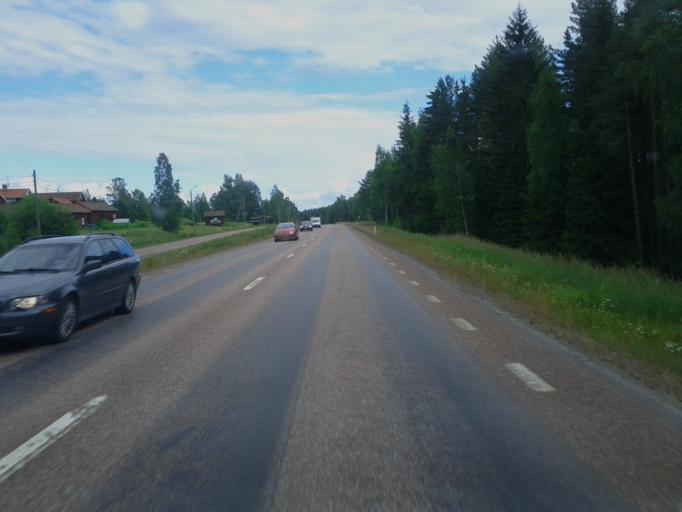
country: SE
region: Dalarna
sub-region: Faluns Kommun
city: Bjursas
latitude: 60.7420
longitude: 15.4022
